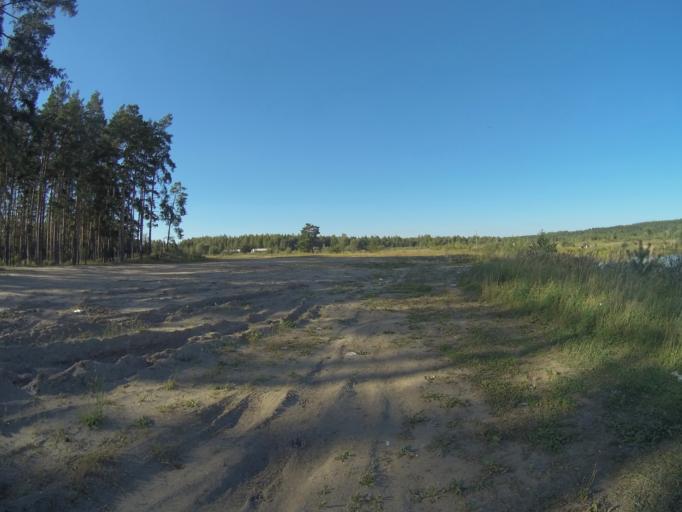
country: RU
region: Vladimir
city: Kommunar
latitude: 56.0506
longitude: 40.4233
